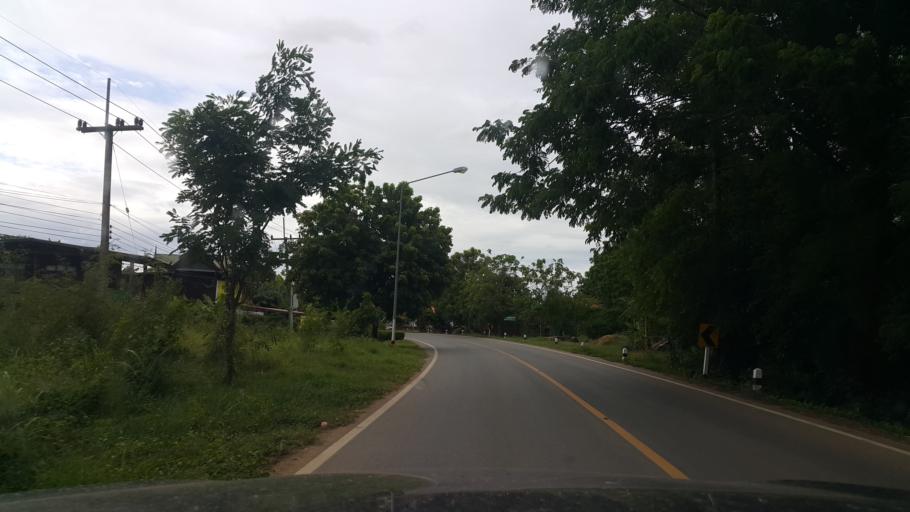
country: TH
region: Sukhothai
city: Ban Na
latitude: 17.0371
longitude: 99.7038
